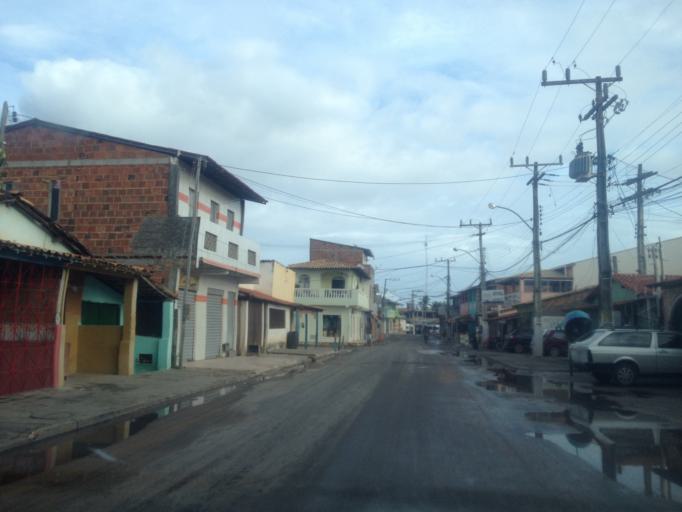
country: BR
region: Bahia
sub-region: Mata De Sao Joao
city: Mata de Sao Joao
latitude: -12.3880
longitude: -37.8823
